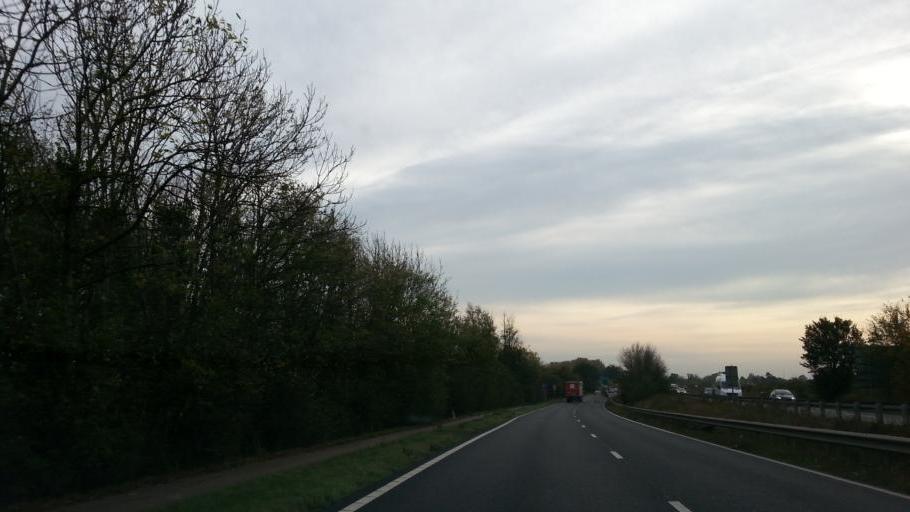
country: GB
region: England
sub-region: Cambridgeshire
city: Buckden
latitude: 52.2748
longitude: -0.2587
